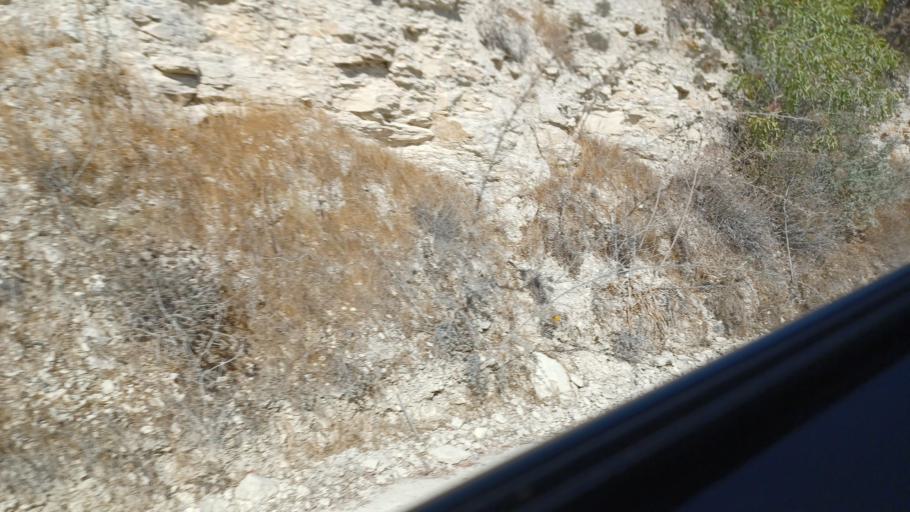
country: CY
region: Pafos
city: Tala
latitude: 34.8656
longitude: 32.4487
